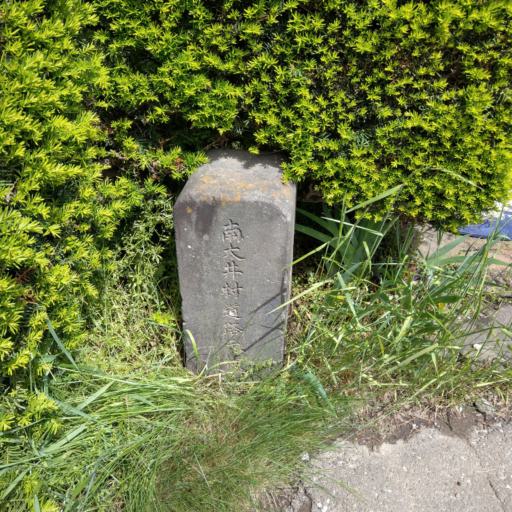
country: JP
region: Nagano
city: Komoro
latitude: 36.3028
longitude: 138.4734
